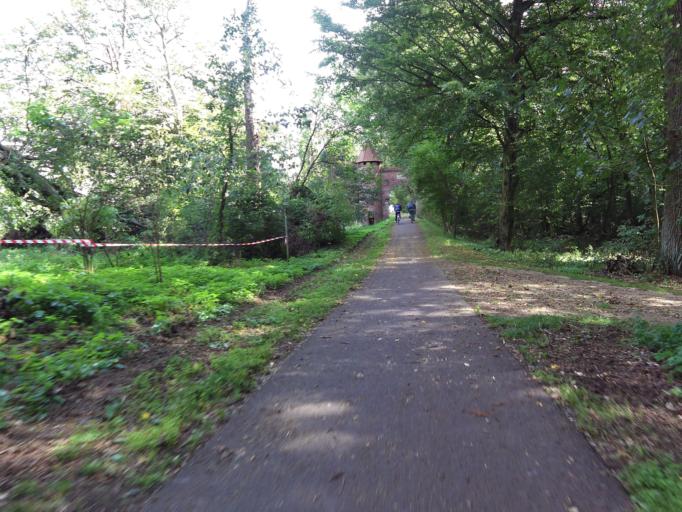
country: DE
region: Saxony-Anhalt
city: Vockerode
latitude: 51.8647
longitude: 12.3268
